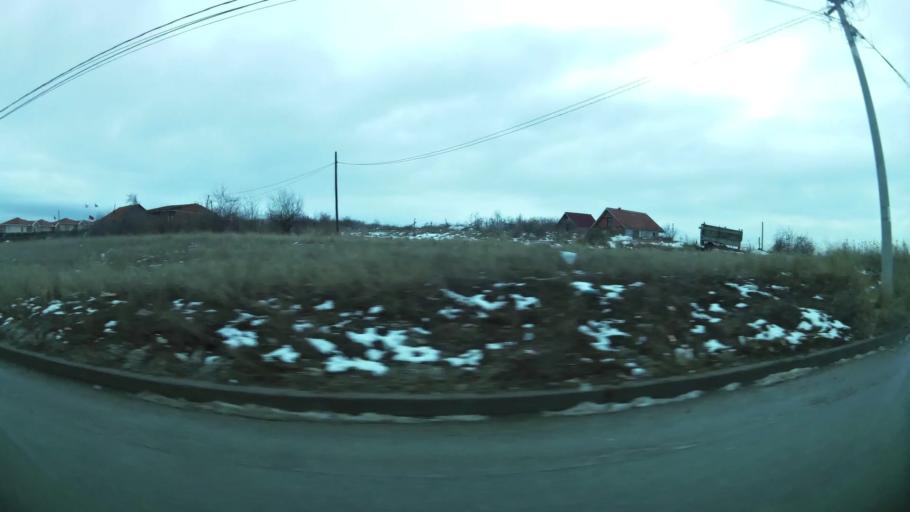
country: XK
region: Pristina
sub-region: Komuna e Prishtines
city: Pristina
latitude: 42.6324
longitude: 21.1683
